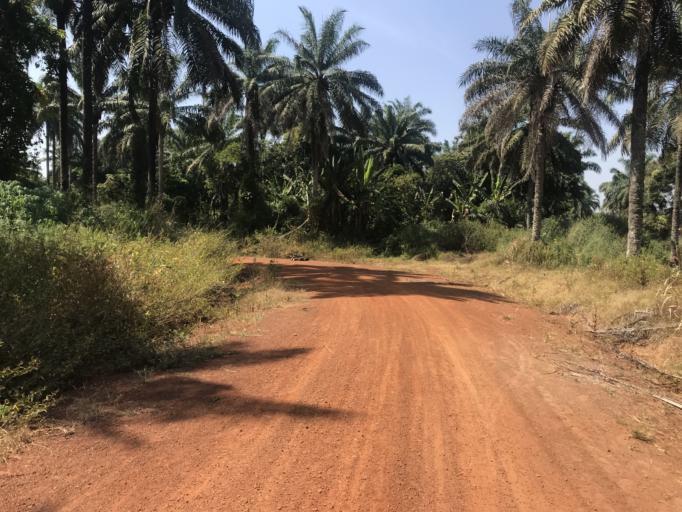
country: NG
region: Osun
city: Ikirun
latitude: 7.9346
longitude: 4.6221
